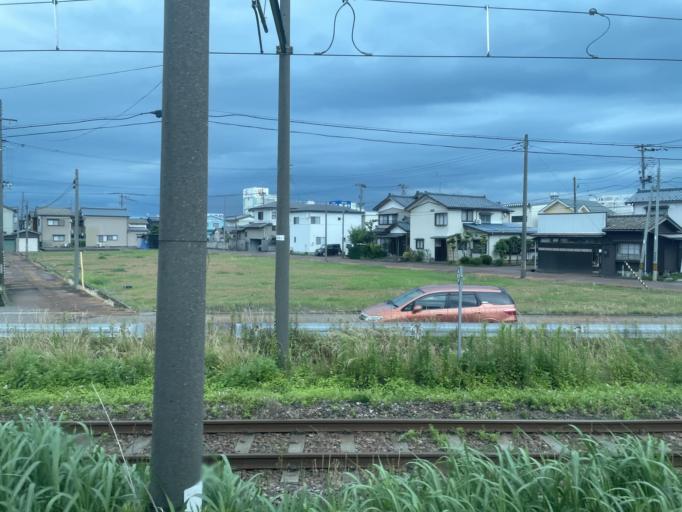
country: JP
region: Niigata
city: Yoshida-kasugacho
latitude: 37.6849
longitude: 138.8750
